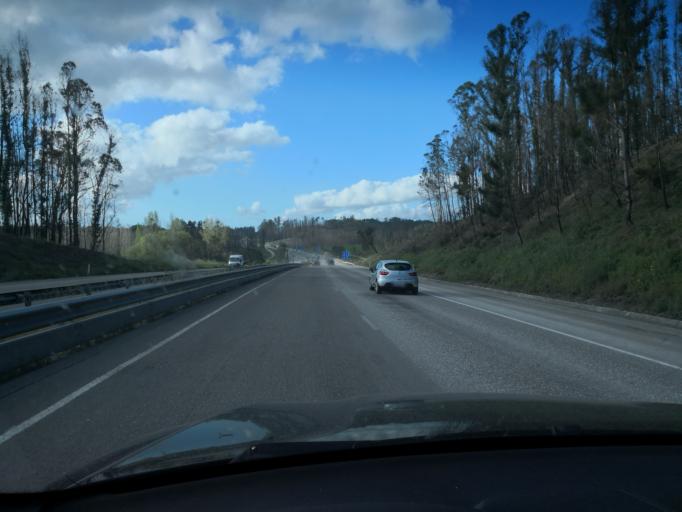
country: PT
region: Aveiro
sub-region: Mealhada
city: Pampilhosa do Botao
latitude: 40.3119
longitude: -8.4894
